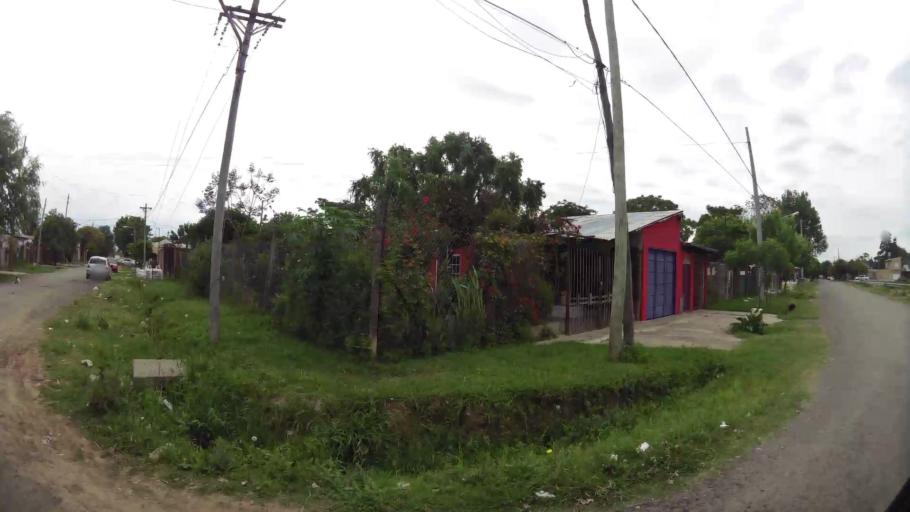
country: AR
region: Buenos Aires
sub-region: Partido de Campana
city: Campana
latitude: -34.1819
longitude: -58.9373
